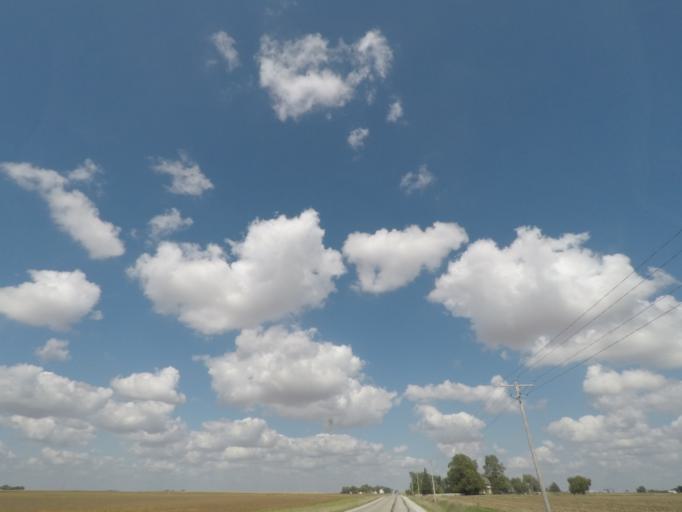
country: US
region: Iowa
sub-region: Story County
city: Nevada
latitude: 42.0609
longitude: -93.4056
